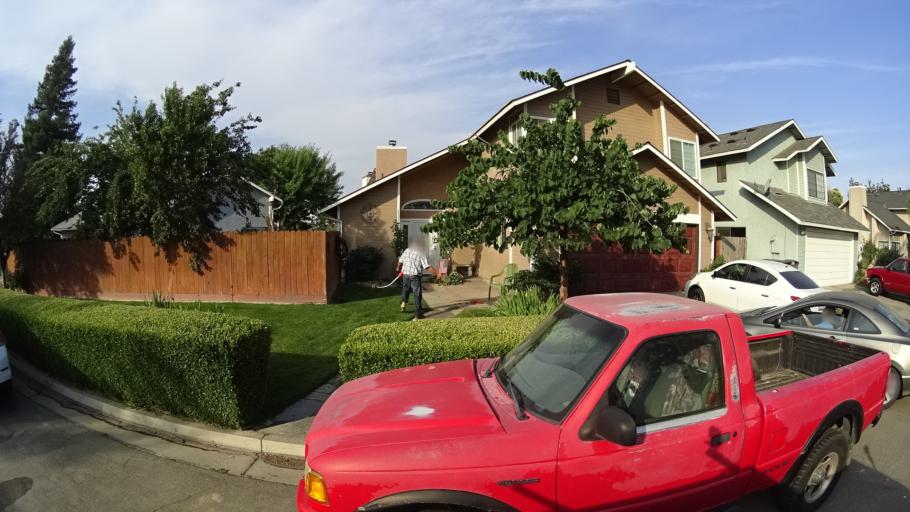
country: US
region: California
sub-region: Fresno County
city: West Park
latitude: 36.7691
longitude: -119.8494
